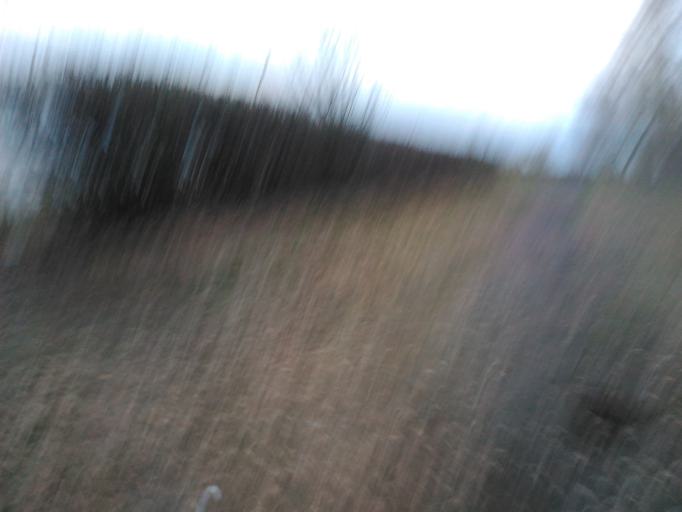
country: RU
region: Ulyanovsk
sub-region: Ulyanovskiy Rayon
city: Ulyanovsk
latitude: 54.3501
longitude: 48.3935
